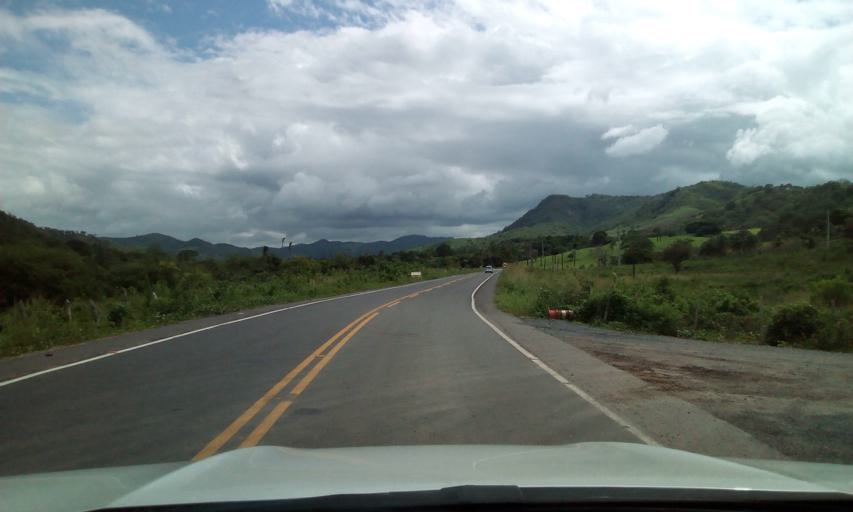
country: BR
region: Paraiba
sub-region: Alagoinha
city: Alagoinha
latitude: -6.8974
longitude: -35.5276
